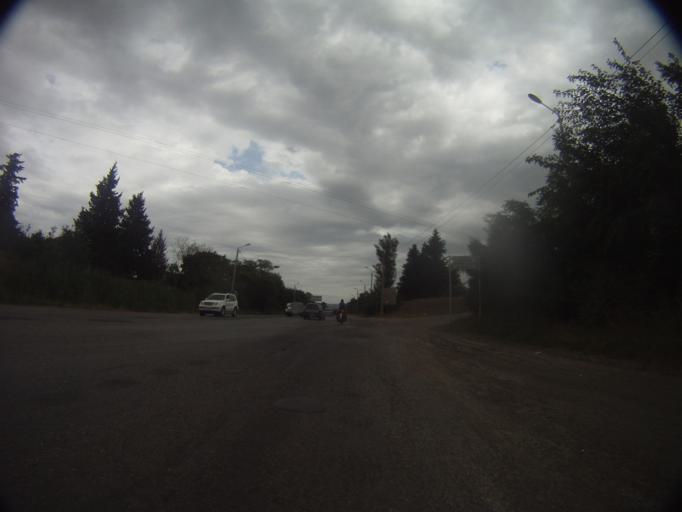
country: GE
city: Didi Lilo
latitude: 41.6898
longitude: 45.0264
